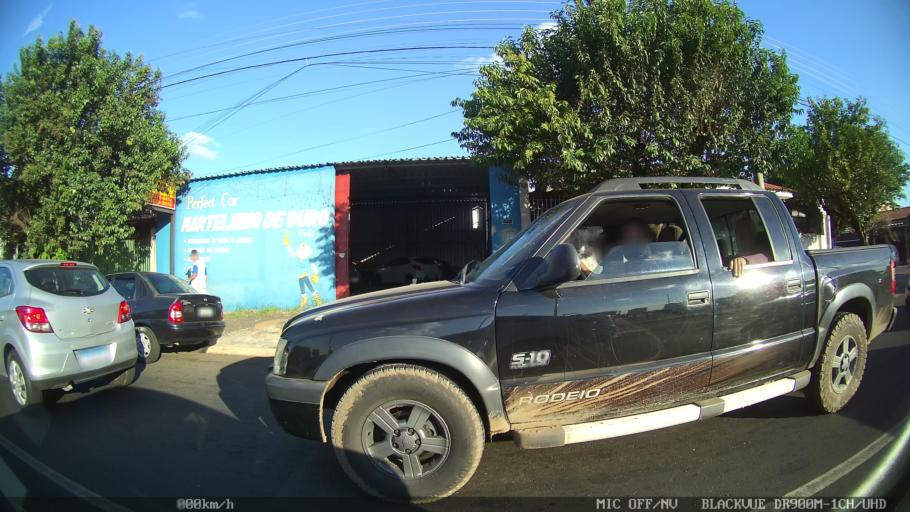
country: BR
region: Sao Paulo
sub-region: Americana
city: Americana
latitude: -22.7386
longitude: -47.3701
